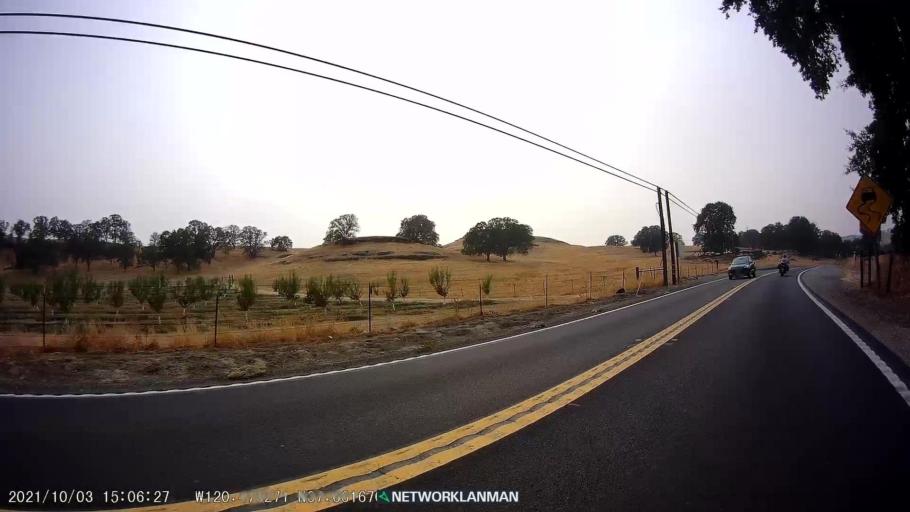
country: US
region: California
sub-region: Stanislaus County
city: Waterford
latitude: 37.6617
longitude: -120.4786
